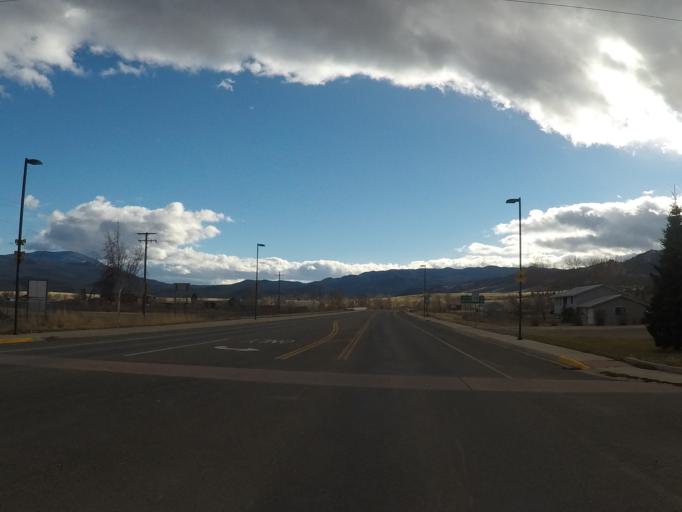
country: US
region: Montana
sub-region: Jefferson County
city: Boulder
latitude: 46.2333
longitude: -112.1206
